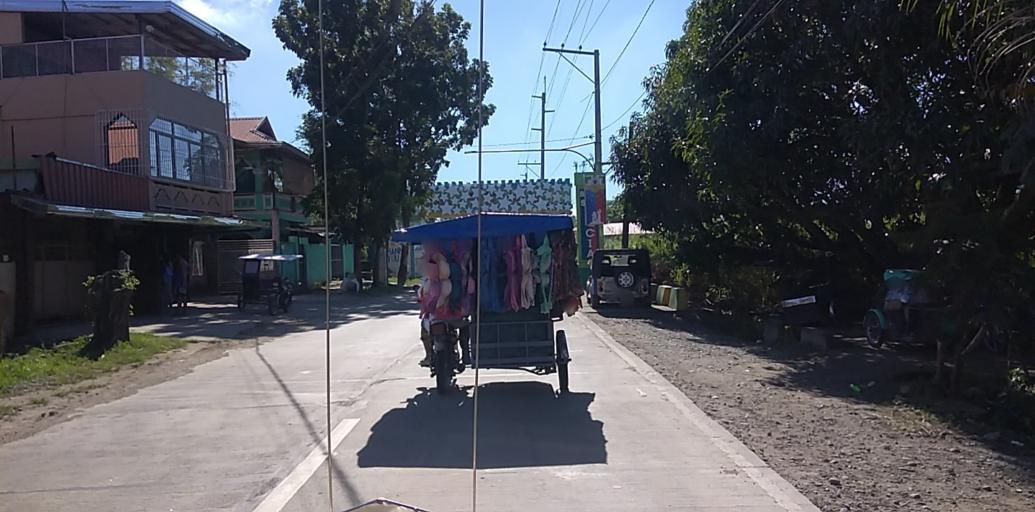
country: PH
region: Central Luzon
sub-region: Province of Pampanga
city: San Luis
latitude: 15.0550
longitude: 120.7781
